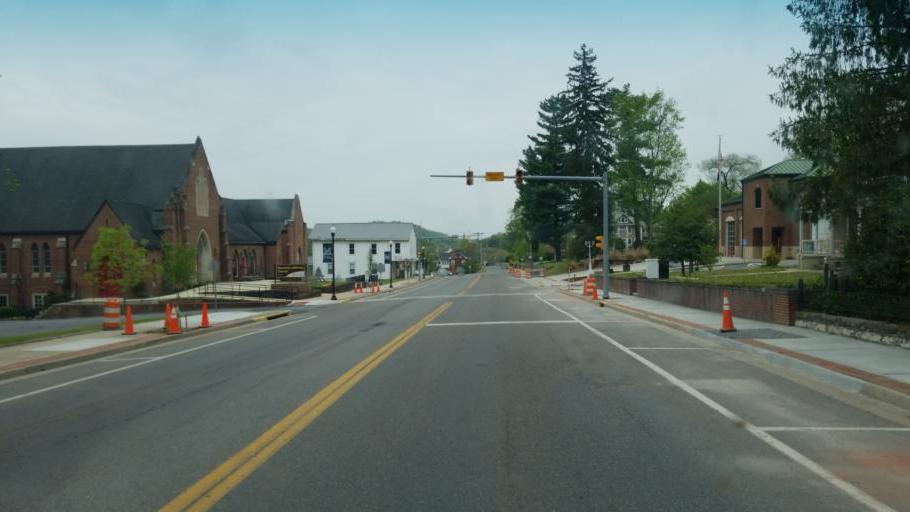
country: US
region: Virginia
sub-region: Smyth County
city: Marion
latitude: 36.8319
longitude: -81.5220
